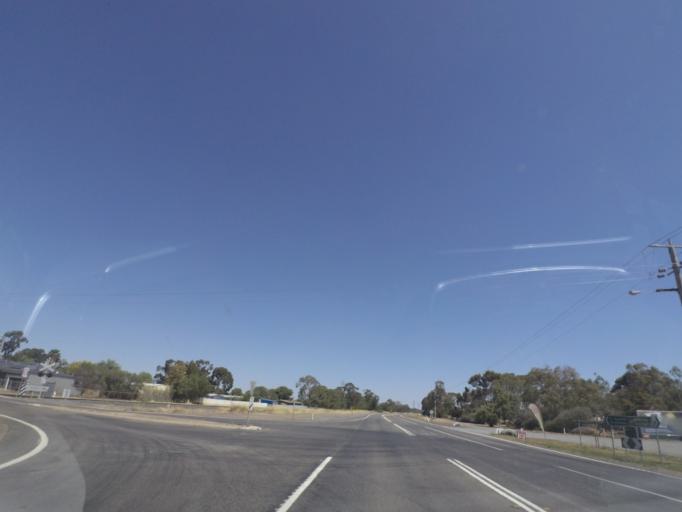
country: AU
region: Victoria
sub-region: Greater Shepparton
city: Shepparton
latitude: -36.2386
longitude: 145.4316
